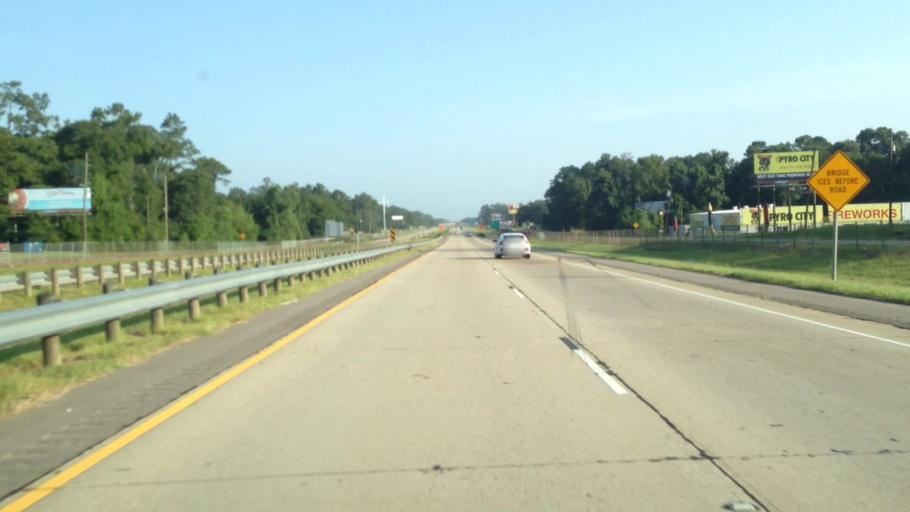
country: US
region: Louisiana
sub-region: Tangipahoa Parish
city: Ponchatoula
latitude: 30.4526
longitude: -90.4705
